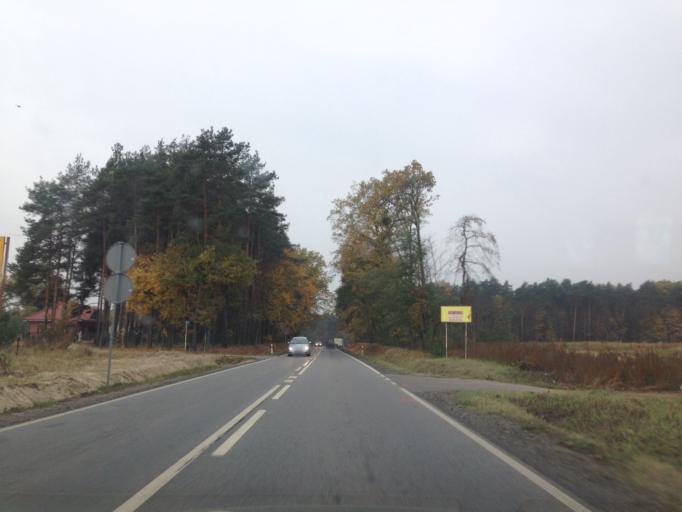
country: PL
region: Kujawsko-Pomorskie
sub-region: Grudziadz
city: Grudziadz
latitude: 53.4436
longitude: 18.8204
